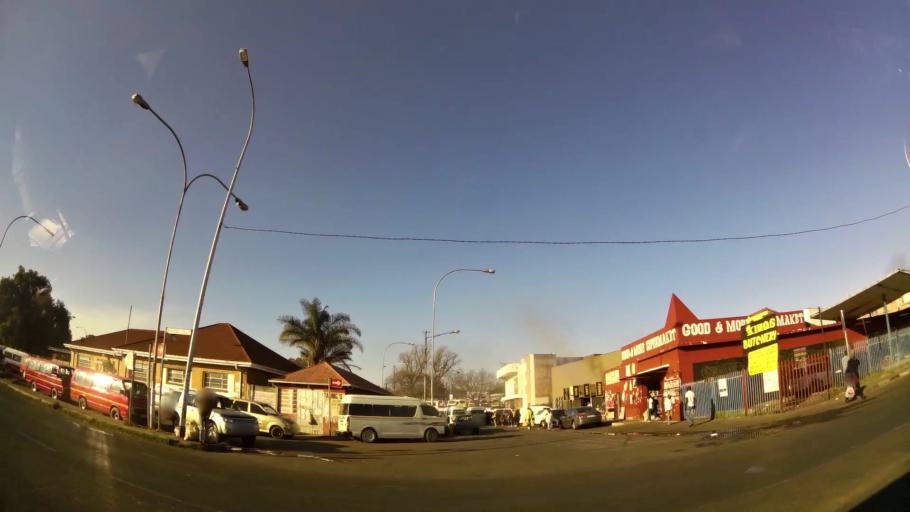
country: ZA
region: Gauteng
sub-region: City of Johannesburg Metropolitan Municipality
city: Roodepoort
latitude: -26.1590
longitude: 27.8687
